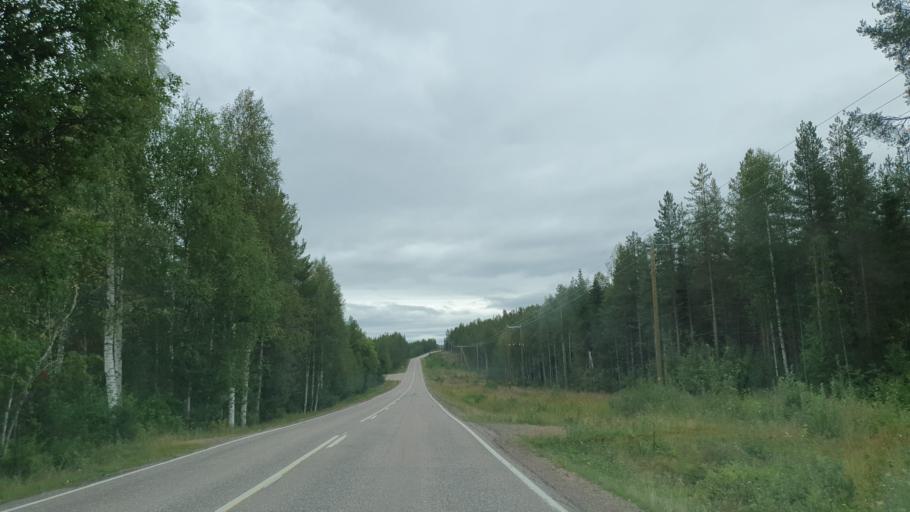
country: FI
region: Lapland
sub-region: Rovaniemi
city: Rovaniemi
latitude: 66.8871
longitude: 25.4056
